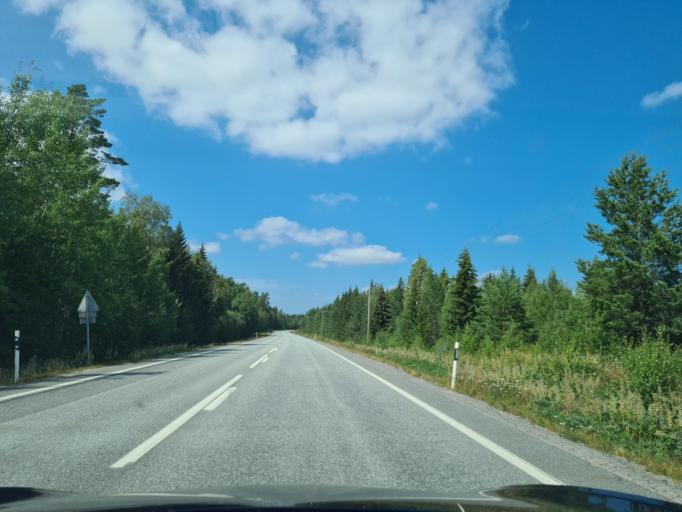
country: FI
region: Ostrobothnia
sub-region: Vaasa
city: Vaasa
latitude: 63.1689
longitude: 21.5861
